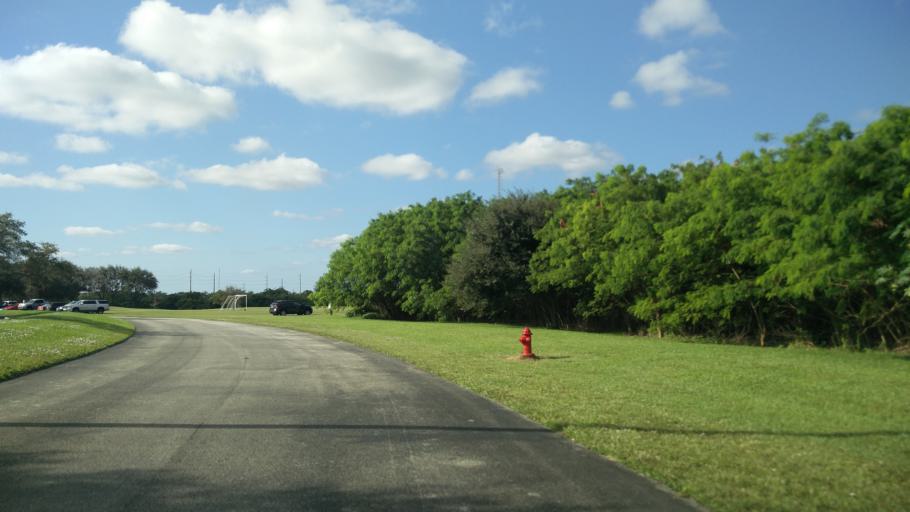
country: US
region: Florida
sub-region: Broward County
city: Rock Island
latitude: 26.1590
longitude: -80.1600
